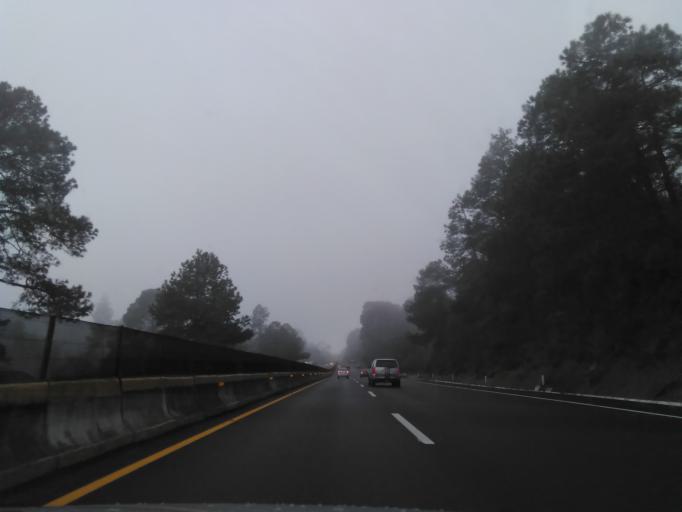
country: MX
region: Morelos
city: Tres Marias
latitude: 19.0998
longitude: -99.2025
